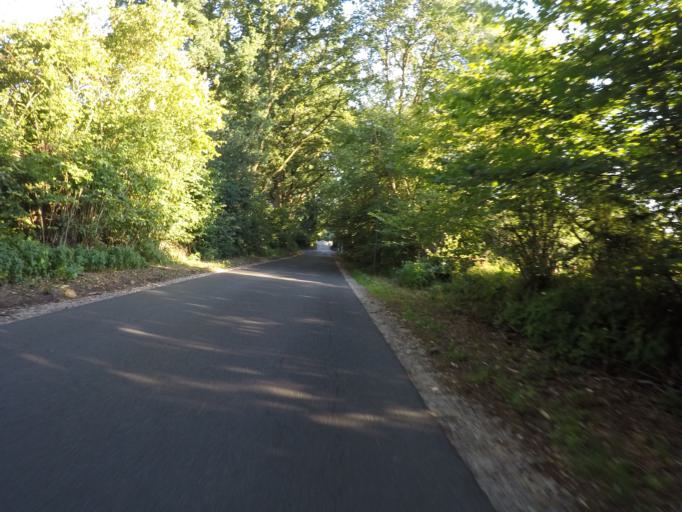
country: DE
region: Hamburg
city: Lemsahl-Mellingstedt
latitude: 53.6922
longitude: 10.1103
